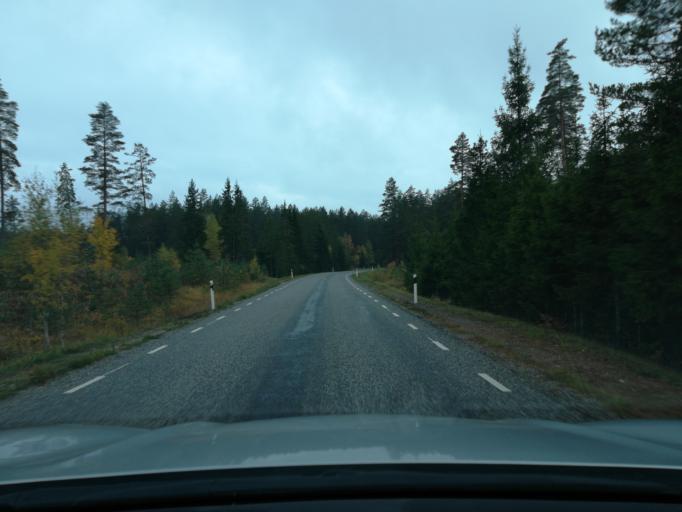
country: EE
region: Ida-Virumaa
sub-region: Johvi vald
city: Johvi
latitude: 59.1713
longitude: 27.4493
